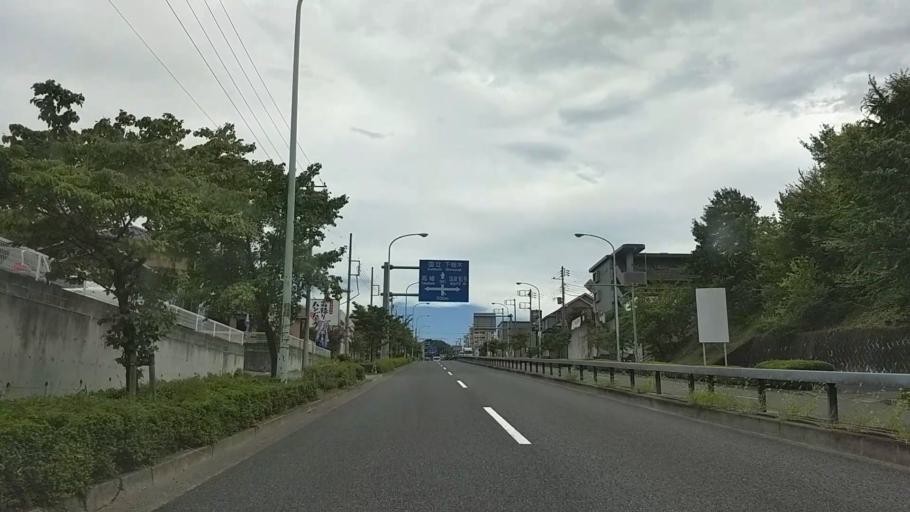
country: JP
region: Tokyo
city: Hachioji
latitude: 35.6418
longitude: 139.3570
